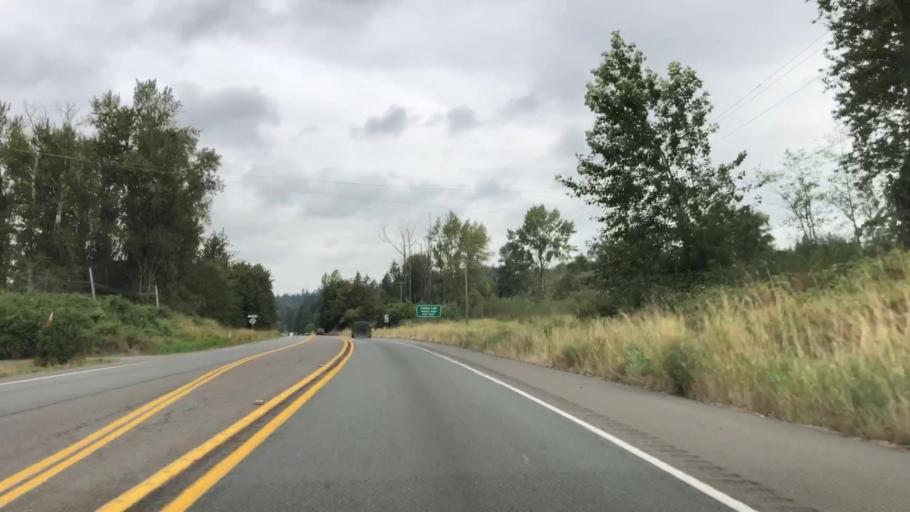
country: US
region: Washington
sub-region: Snohomish County
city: Three Lakes
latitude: 47.9016
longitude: -122.0376
